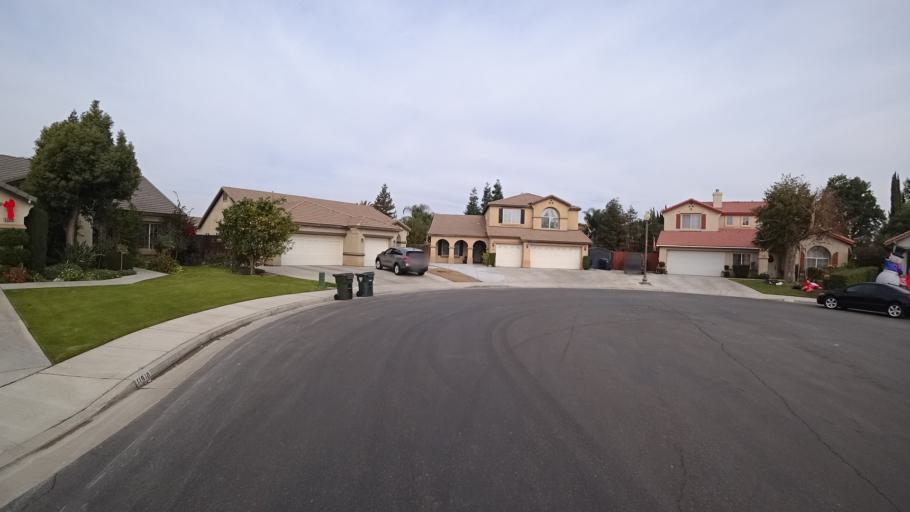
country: US
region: California
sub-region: Kern County
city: Rosedale
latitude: 35.3424
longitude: -119.1352
